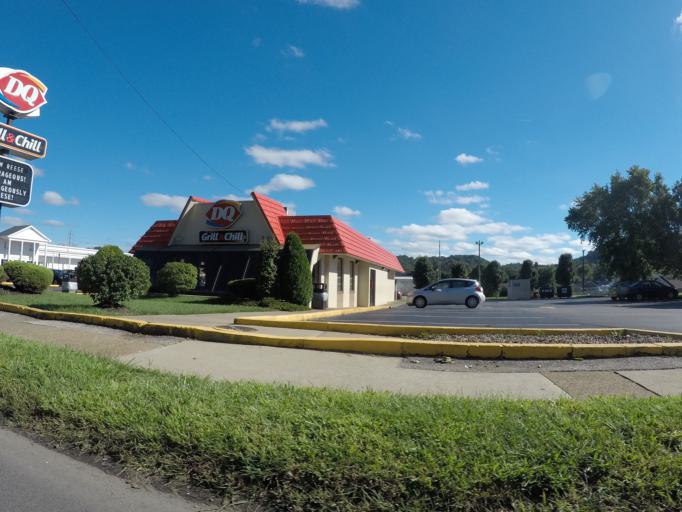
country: US
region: West Virginia
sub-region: Cabell County
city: Huntington
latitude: 38.4094
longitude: -82.4890
